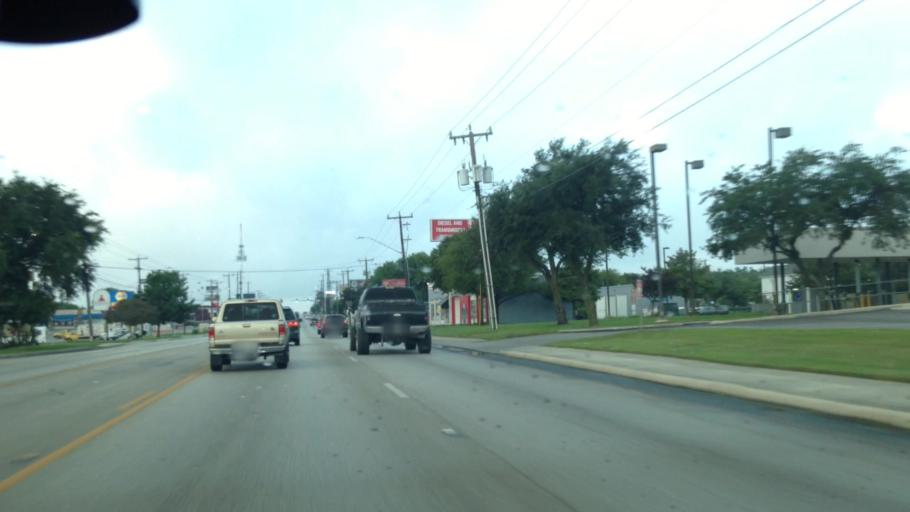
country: US
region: Texas
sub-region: Bexar County
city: Windcrest
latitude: 29.5591
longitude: -98.3964
